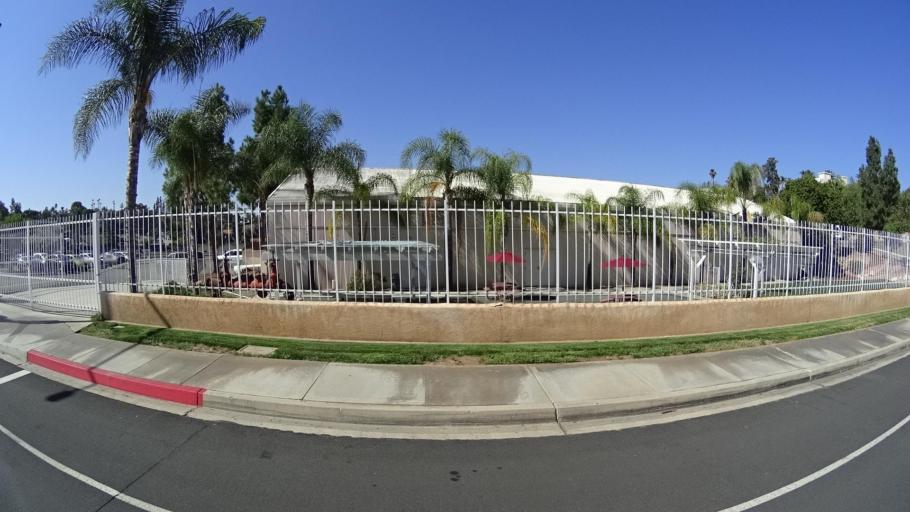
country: US
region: California
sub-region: San Diego County
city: Granite Hills
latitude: 32.7989
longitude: -116.9037
